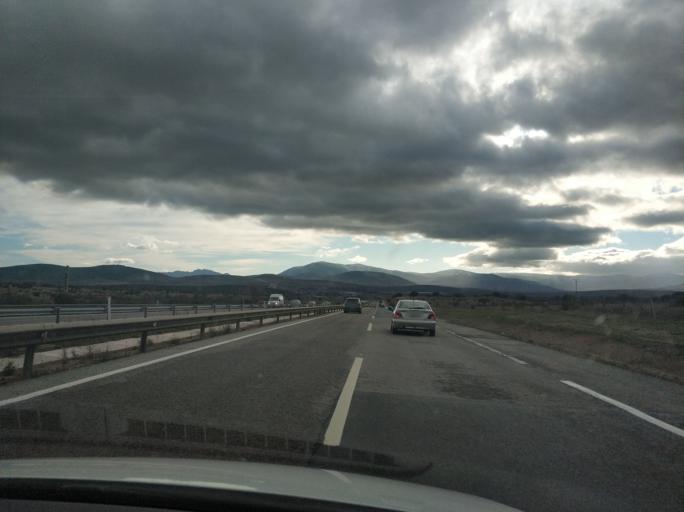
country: ES
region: Madrid
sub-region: Provincia de Madrid
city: Gascones
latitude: 41.0188
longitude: -3.6275
